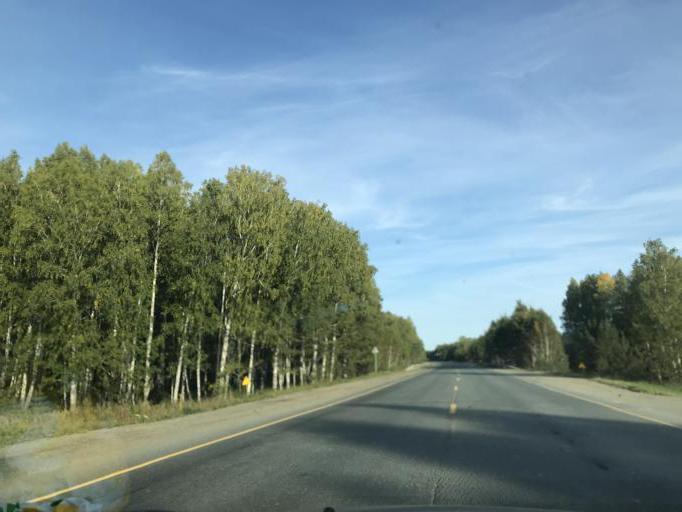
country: RU
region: Chelyabinsk
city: Sargazy
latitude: 54.9714
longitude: 61.2200
